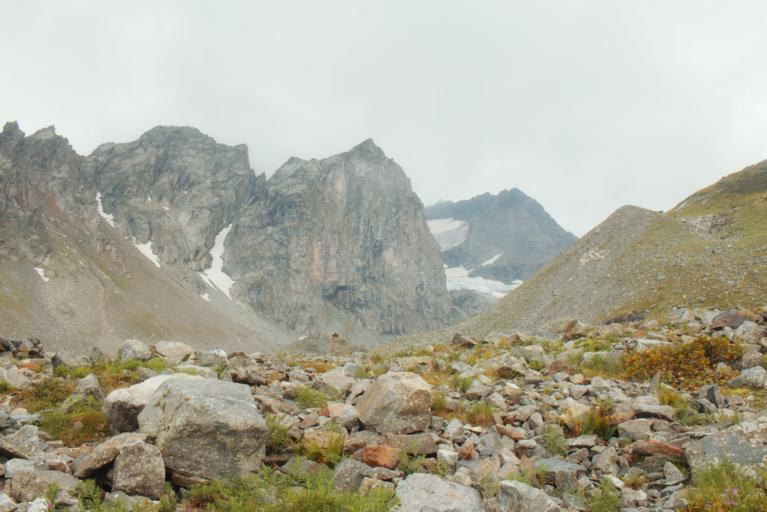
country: RU
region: Karachayevo-Cherkesiya
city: Nizhniy Arkhyz
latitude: 43.4380
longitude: 41.2577
